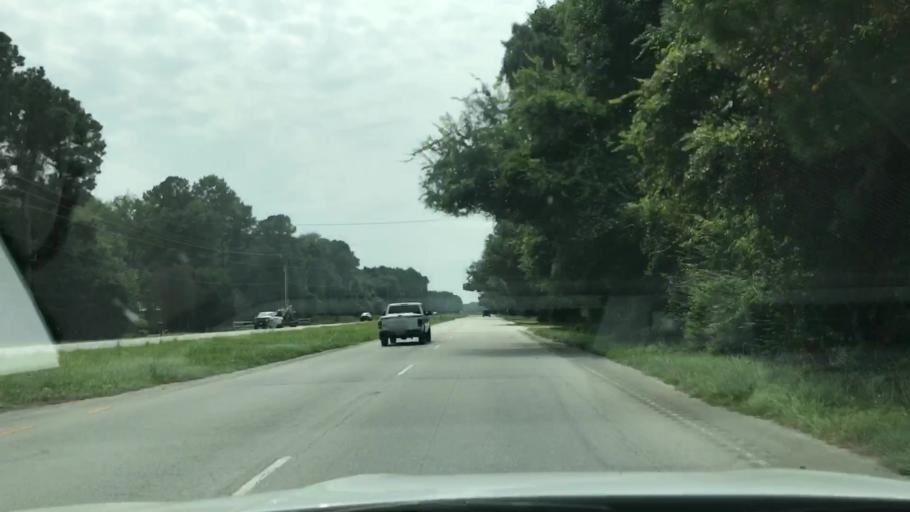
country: US
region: South Carolina
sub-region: Charleston County
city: Awendaw
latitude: 32.9869
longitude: -79.6497
